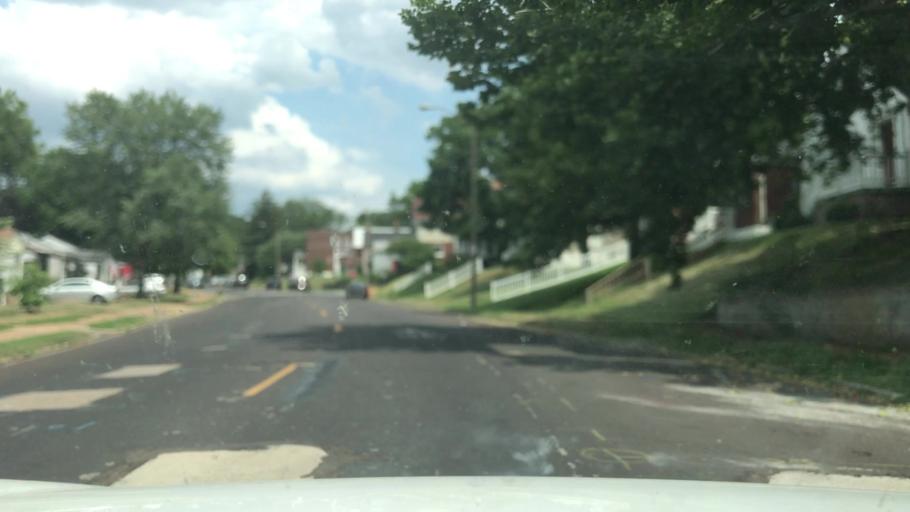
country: US
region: Missouri
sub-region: Saint Louis County
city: Maplewood
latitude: 38.6124
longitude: -90.2996
